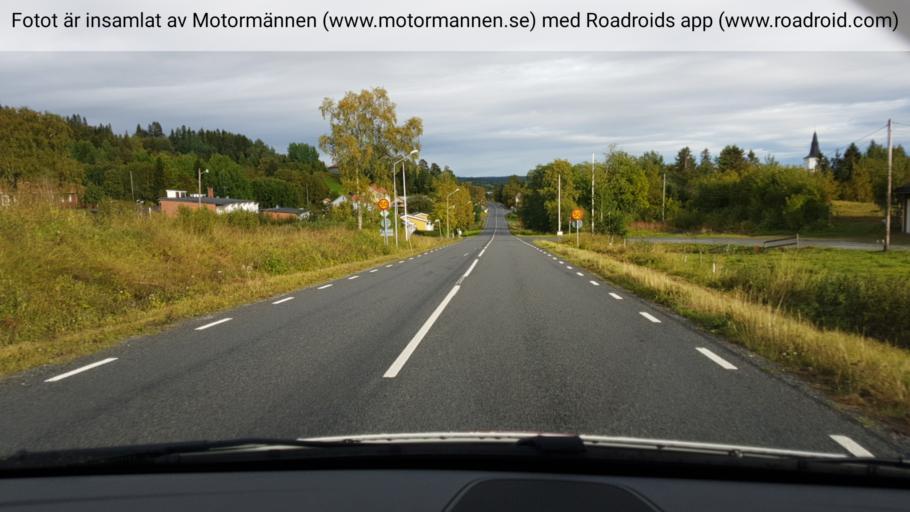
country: SE
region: Jaemtland
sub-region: Are Kommun
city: Are
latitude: 63.4741
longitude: 13.2242
